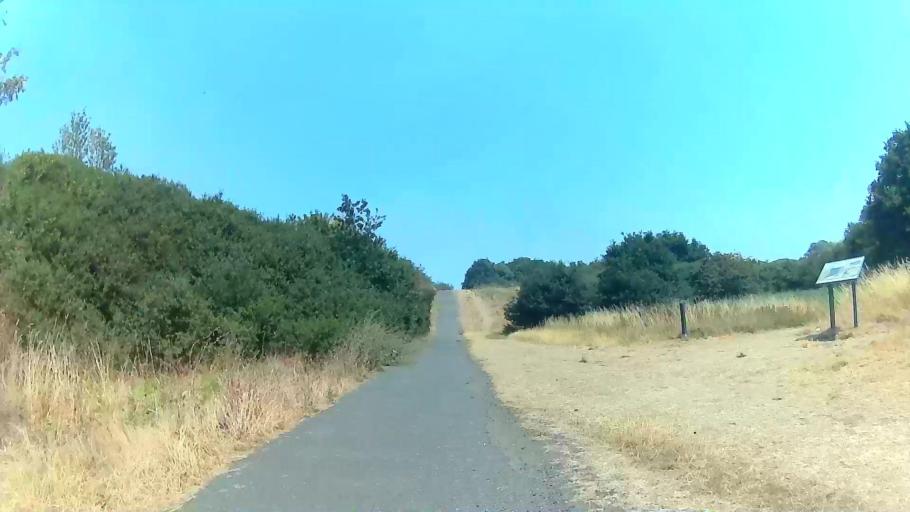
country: GB
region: England
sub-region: Greater London
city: Elm Park
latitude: 51.5356
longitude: 0.2133
